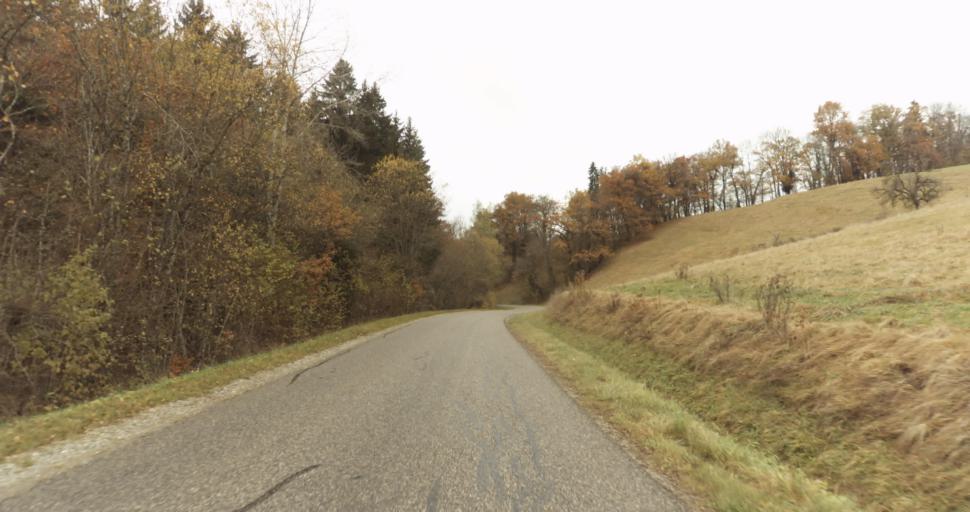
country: FR
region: Rhone-Alpes
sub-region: Departement de la Haute-Savoie
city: Groisy
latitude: 46.0140
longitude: 6.1604
